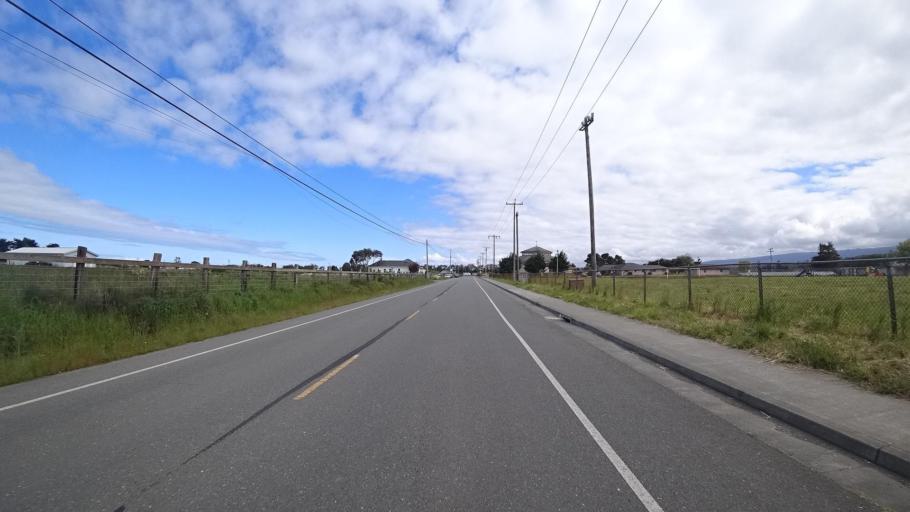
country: US
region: California
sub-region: Humboldt County
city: Arcata
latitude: 40.8768
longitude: -124.1012
